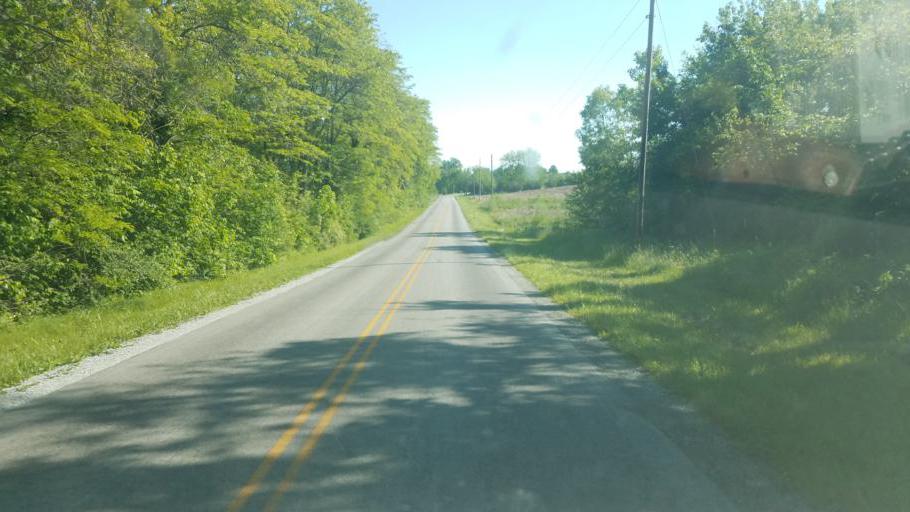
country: US
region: Ohio
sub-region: Hardin County
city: Kenton
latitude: 40.5746
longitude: -83.6326
